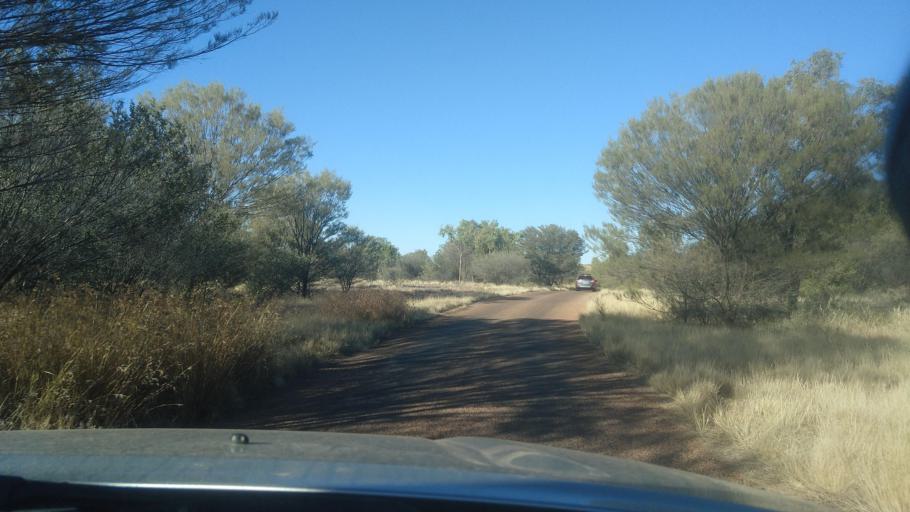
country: AU
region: Northern Territory
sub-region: Alice Springs
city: Alice Springs
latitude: -23.7042
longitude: 133.8320
